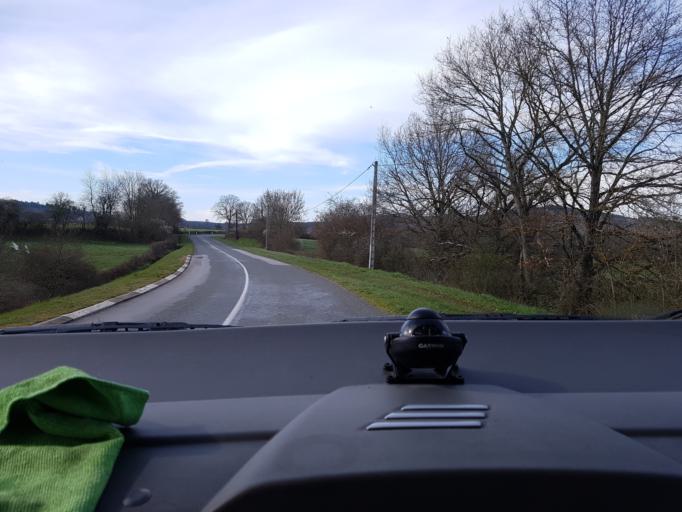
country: FR
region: Bourgogne
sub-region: Departement de Saone-et-Loire
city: Toulon-sur-Arroux
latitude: 46.7521
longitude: 4.1308
